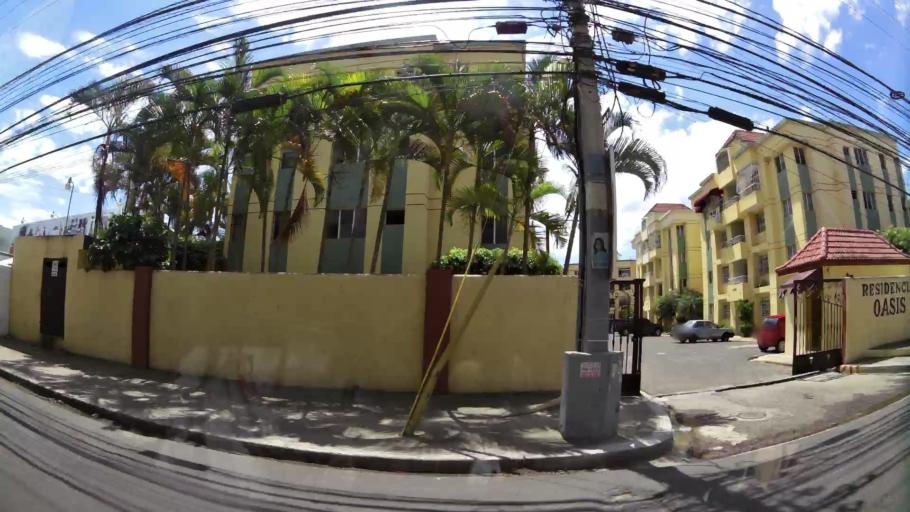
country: DO
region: Santiago
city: Santiago de los Caballeros
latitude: 19.4593
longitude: -70.6644
